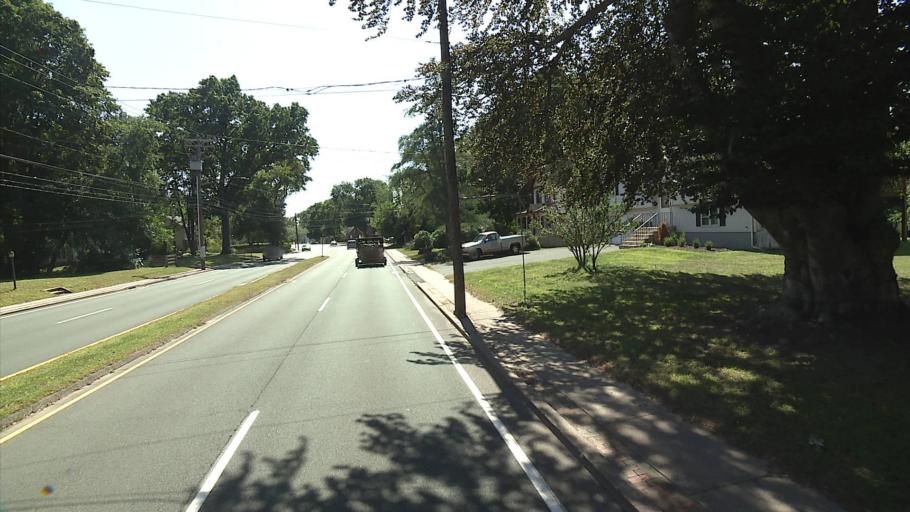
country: US
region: Connecticut
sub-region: Hartford County
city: Windsor
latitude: 41.8314
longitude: -72.6550
